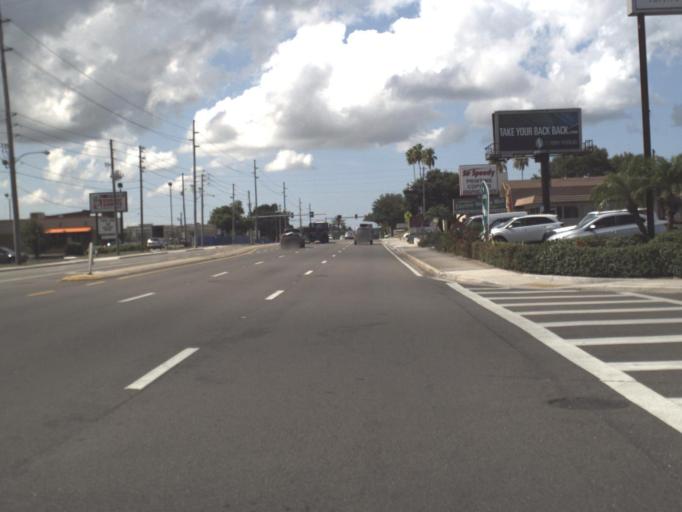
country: US
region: Florida
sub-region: Pinellas County
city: Largo
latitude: 27.9227
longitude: -82.7878
